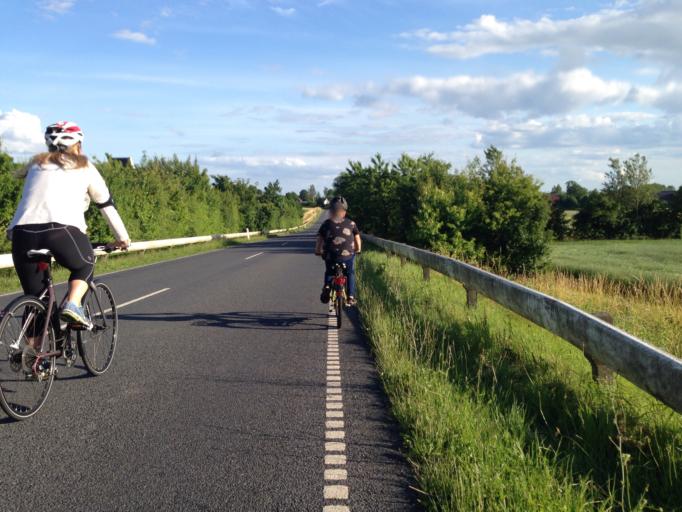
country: DK
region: South Denmark
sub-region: Middelfart Kommune
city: Norre Aby
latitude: 55.4864
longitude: 9.9023
